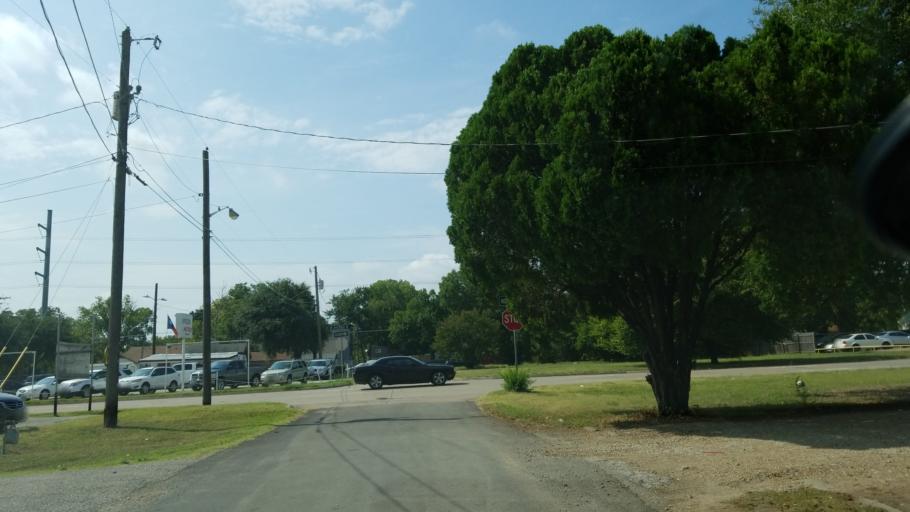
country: US
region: Texas
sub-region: Dallas County
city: Garland
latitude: 32.9111
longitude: -96.6333
